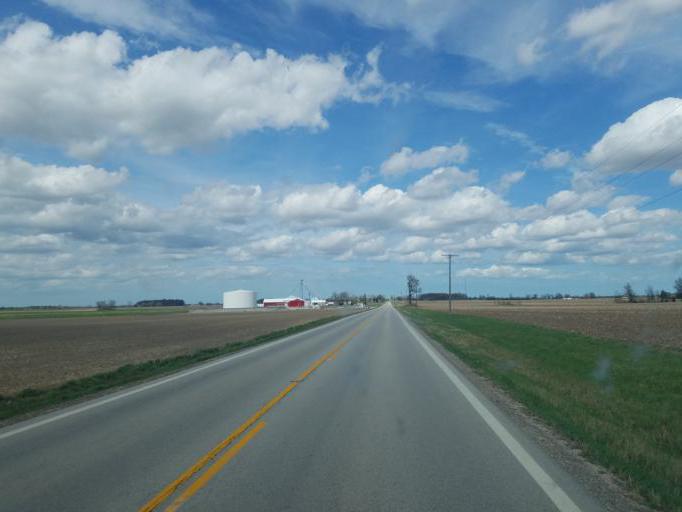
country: US
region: Ohio
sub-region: Huron County
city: Bellevue
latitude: 41.2496
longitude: -82.8019
